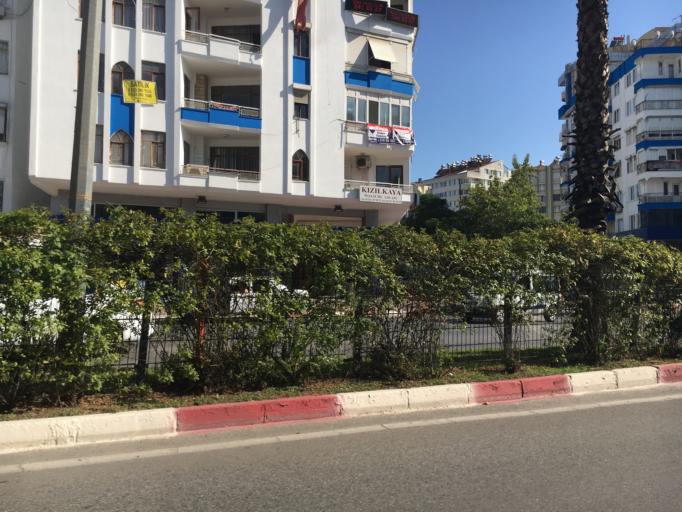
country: TR
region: Antalya
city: Antalya
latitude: 36.8919
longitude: 30.6981
